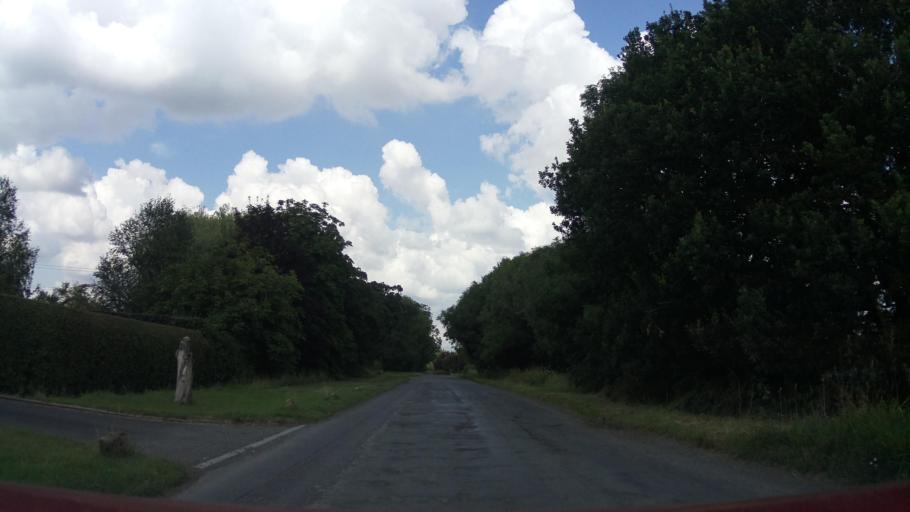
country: GB
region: England
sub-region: Wiltshire
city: Hankerton
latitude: 51.5853
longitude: -2.0153
